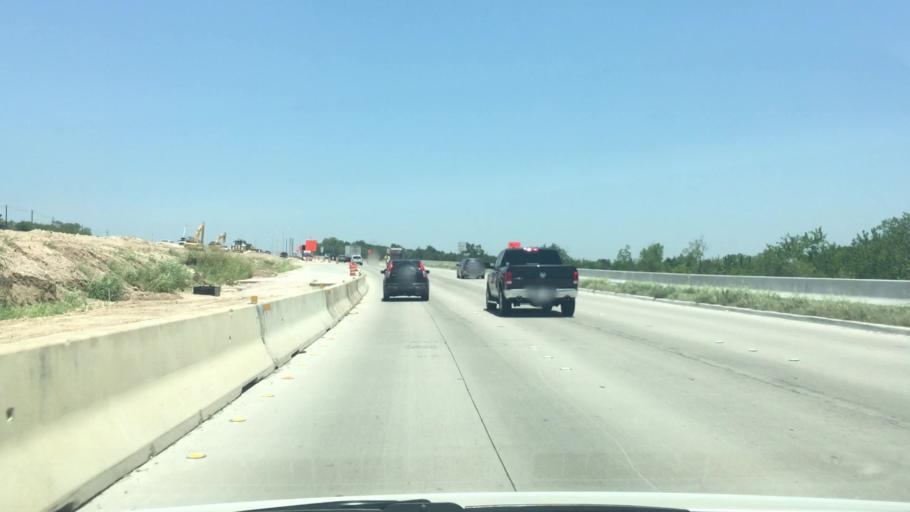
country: US
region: Texas
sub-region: Travis County
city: Austin
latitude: 30.3058
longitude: -97.6602
